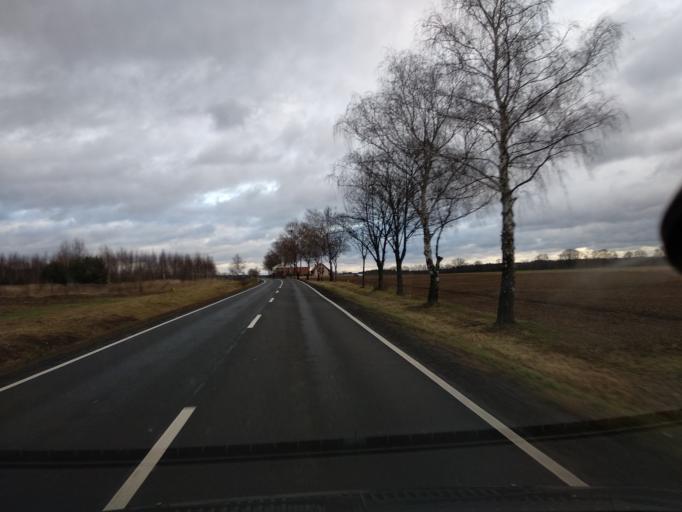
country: PL
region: Lower Silesian Voivodeship
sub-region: Powiat olesnicki
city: Miedzyborz
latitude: 51.3419
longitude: 17.5898
